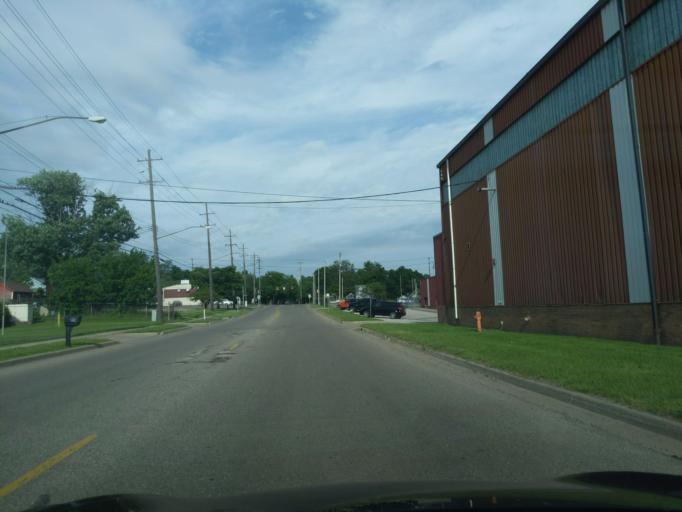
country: US
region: Michigan
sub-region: Ingham County
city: Lansing
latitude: 42.7231
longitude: -84.5406
